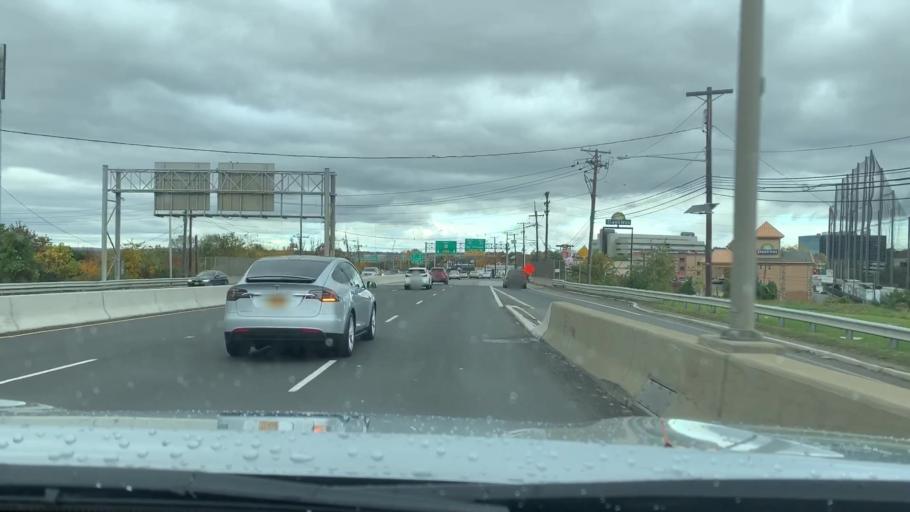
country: US
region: New Jersey
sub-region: Bergen County
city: Palisades Park
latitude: 40.8439
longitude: -74.0062
